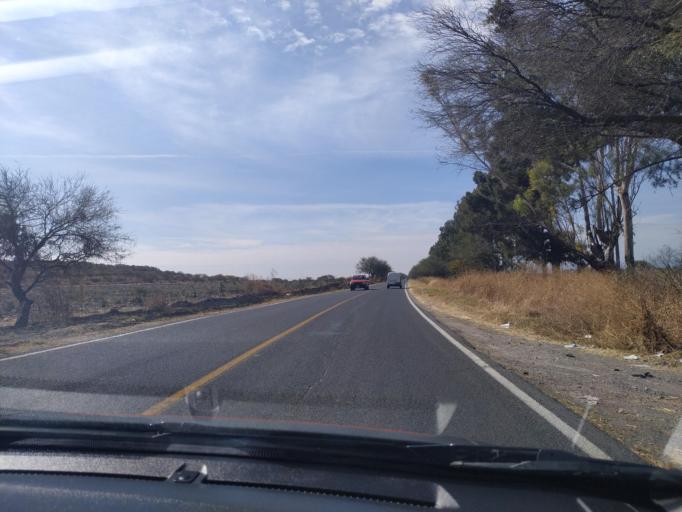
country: MX
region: Guanajuato
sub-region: San Francisco del Rincon
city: San Ignacio de Hidalgo
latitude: 20.9282
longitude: -101.8518
